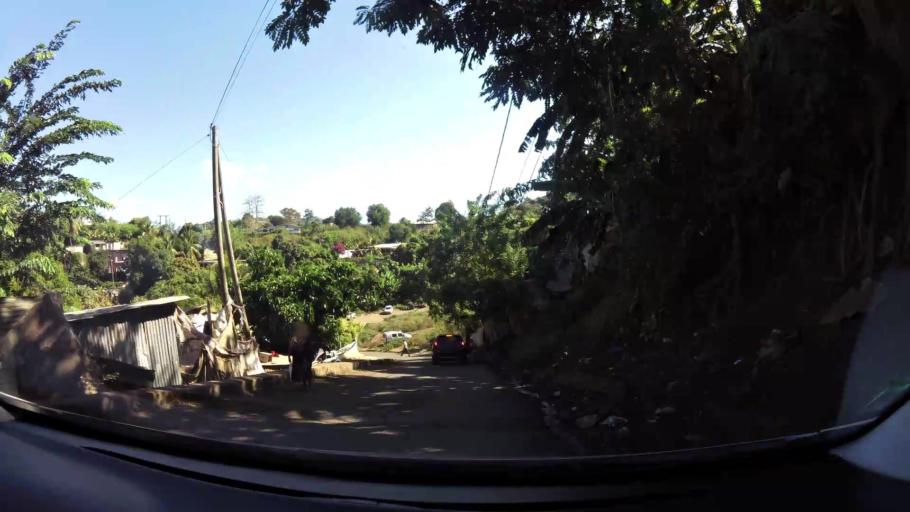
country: YT
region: Mamoudzou
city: Mamoudzou
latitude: -12.7898
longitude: 45.2175
